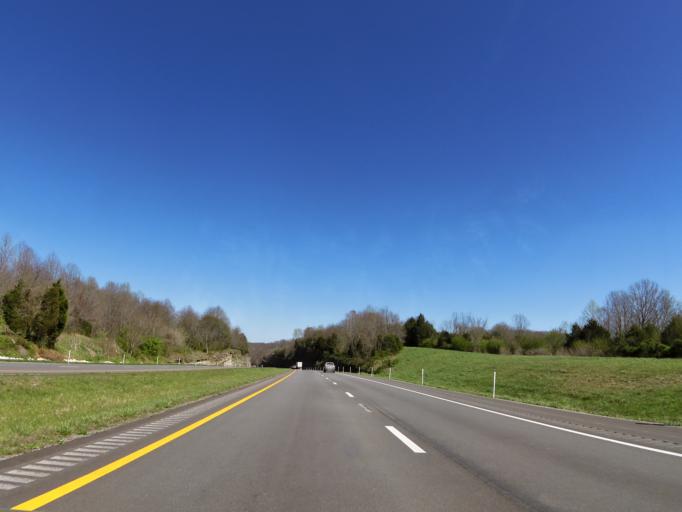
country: US
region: Kentucky
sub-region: Pulaski County
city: Somerset
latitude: 37.0958
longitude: -84.7150
